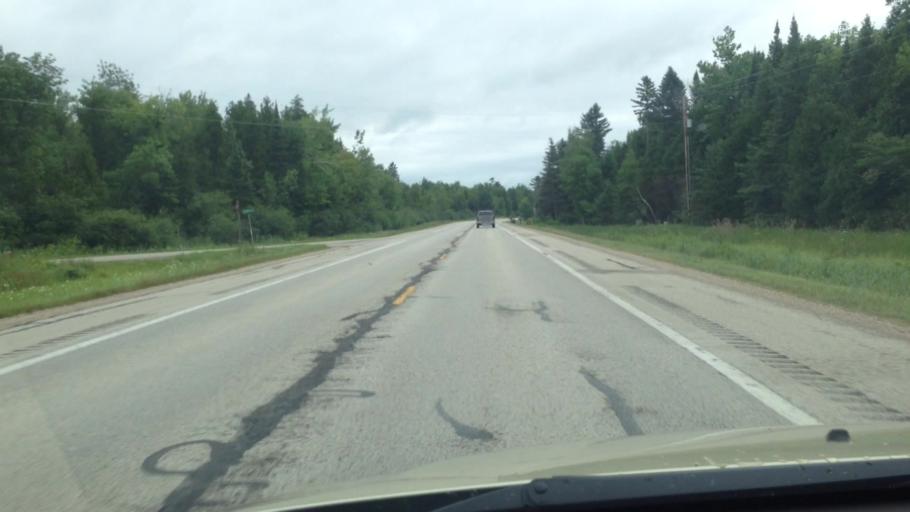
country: US
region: Michigan
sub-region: Delta County
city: Escanaba
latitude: 45.6657
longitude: -87.1680
